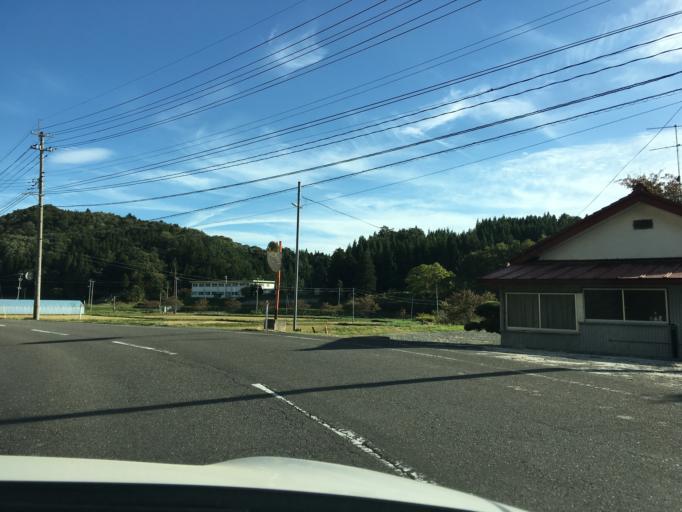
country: JP
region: Fukushima
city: Funehikimachi-funehiki
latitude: 37.3173
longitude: 140.6005
